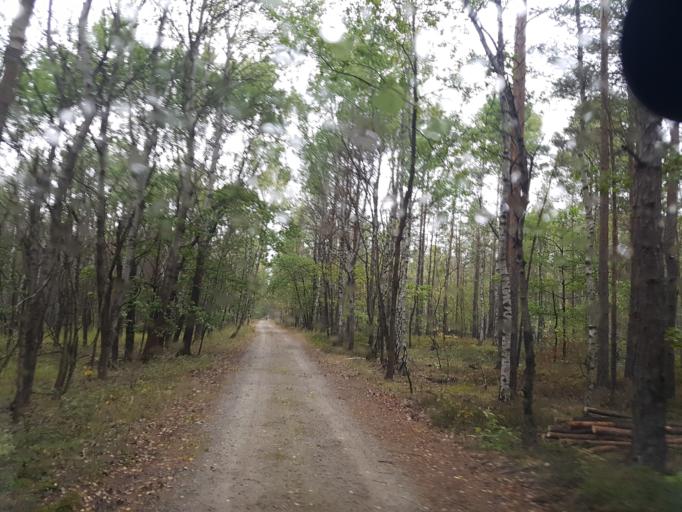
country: DE
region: Brandenburg
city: Sallgast
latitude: 51.6073
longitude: 13.7785
